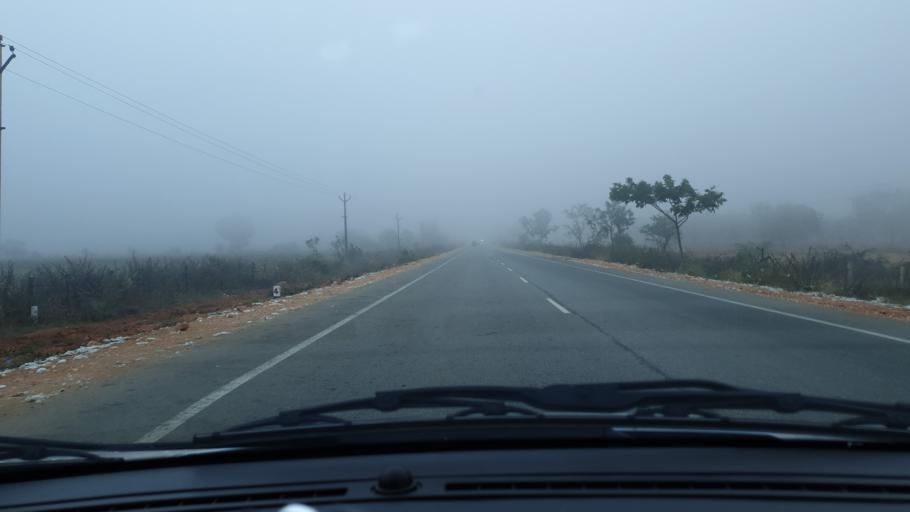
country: IN
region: Telangana
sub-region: Mahbubnagar
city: Nagar Karnul
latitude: 16.6359
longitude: 78.6007
